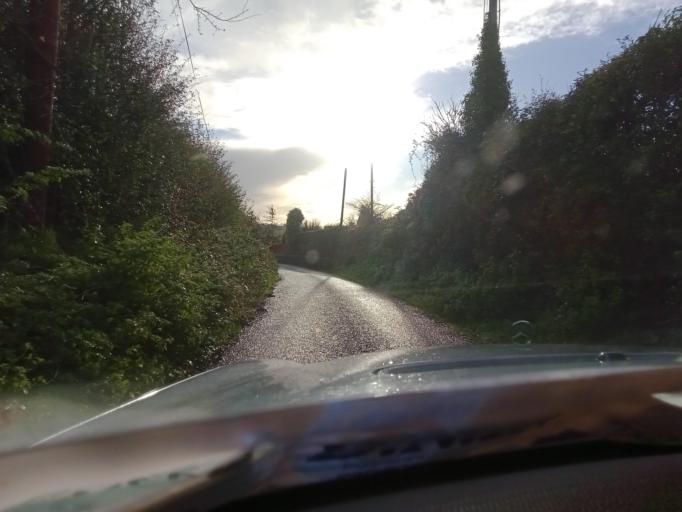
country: IE
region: Leinster
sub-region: Kilkenny
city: Mooncoin
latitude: 52.2749
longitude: -7.1829
